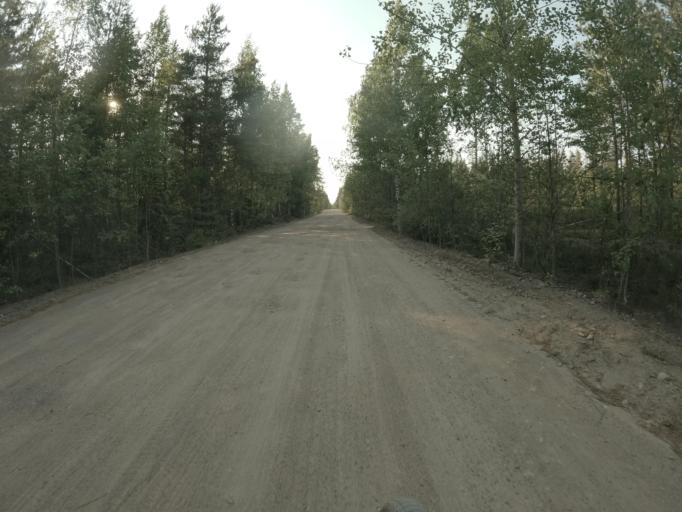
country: RU
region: Leningrad
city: Veshchevo
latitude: 60.4579
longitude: 29.2474
